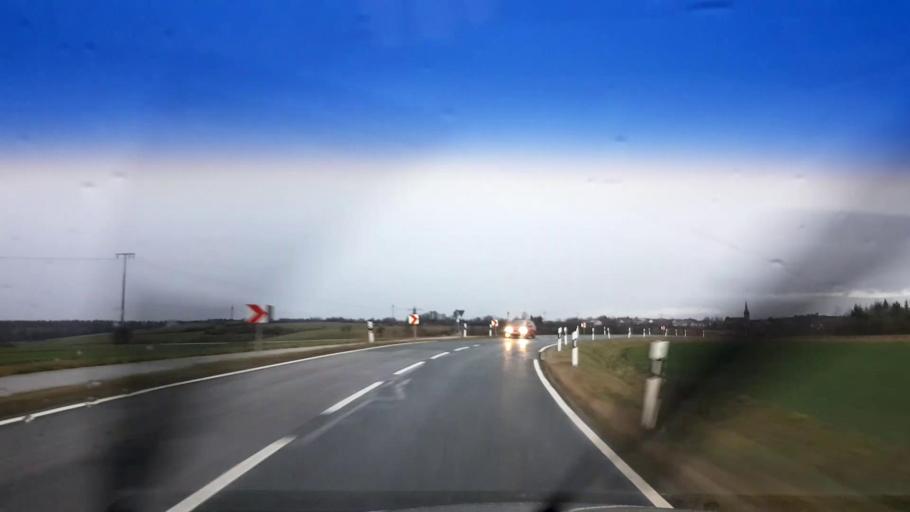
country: DE
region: Bavaria
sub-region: Upper Franconia
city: Litzendorf
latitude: 49.8726
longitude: 11.0208
